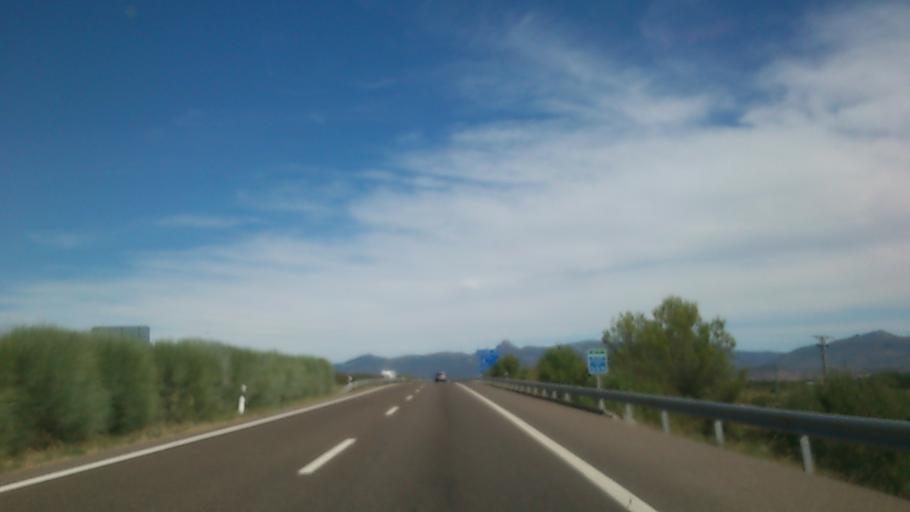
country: ES
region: Aragon
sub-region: Provincia de Huesca
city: Huesca
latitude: 42.1366
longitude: -0.4300
